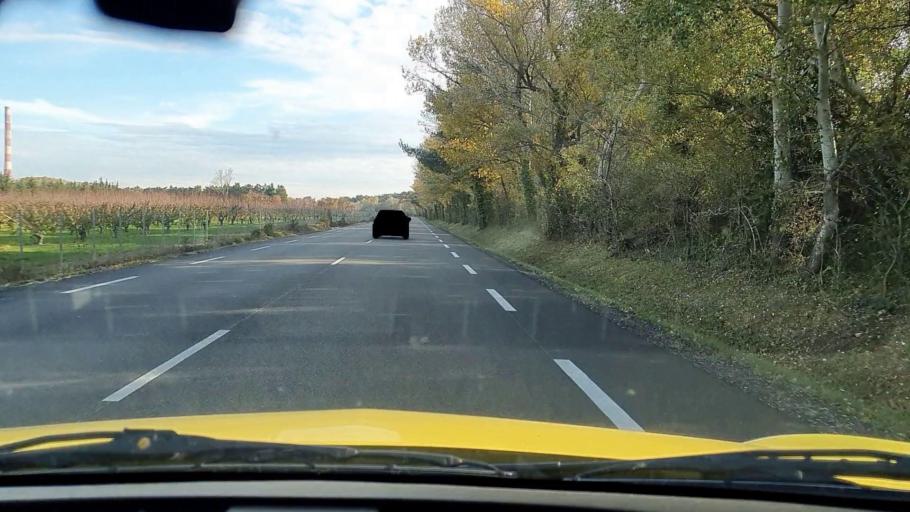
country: FR
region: Languedoc-Roussillon
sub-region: Departement du Gard
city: Vallabregues
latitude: 43.8715
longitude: 4.6353
